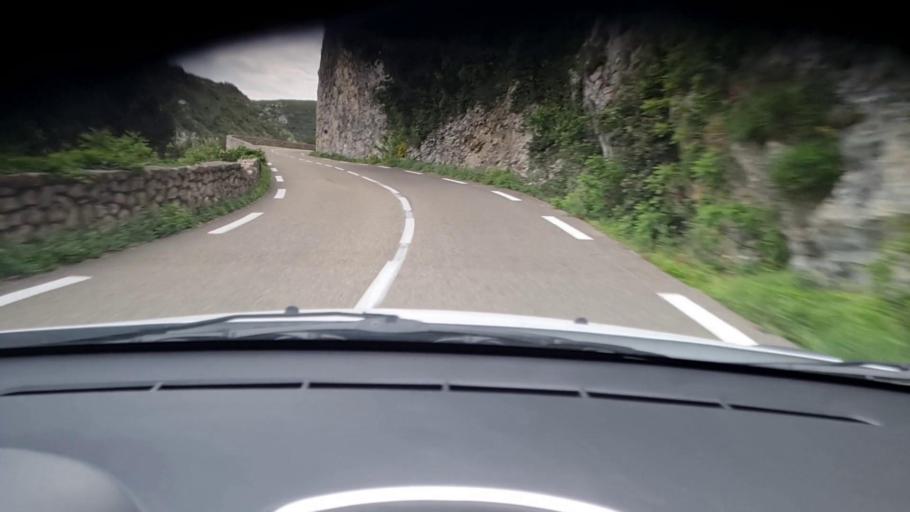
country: FR
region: Languedoc-Roussillon
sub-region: Departement du Gard
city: Blauzac
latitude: 43.9381
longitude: 4.3833
